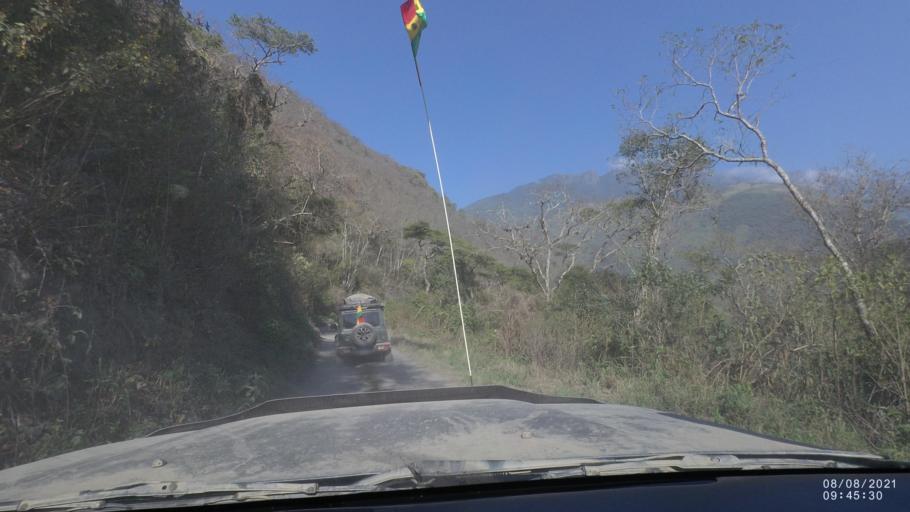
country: BO
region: La Paz
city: Quime
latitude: -16.6041
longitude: -66.7266
